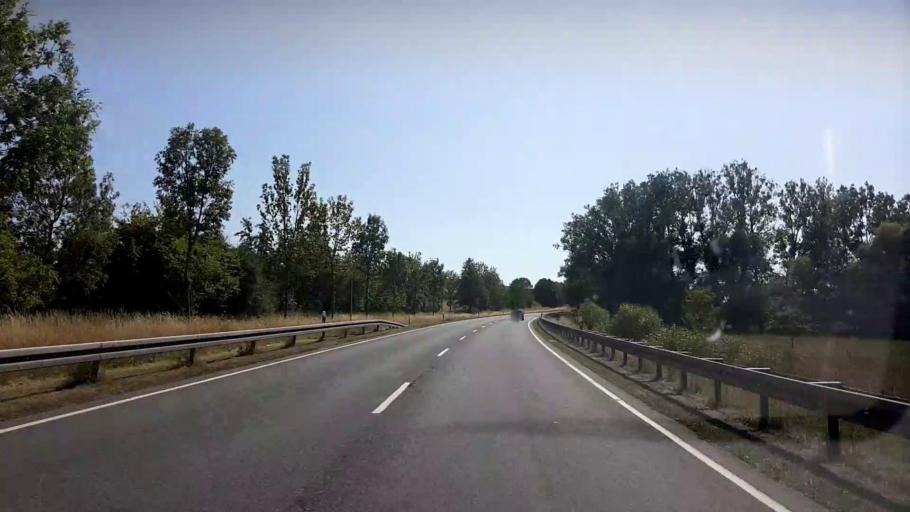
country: DE
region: Bavaria
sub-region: Upper Franconia
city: Grossheirath
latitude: 50.1579
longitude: 10.9306
